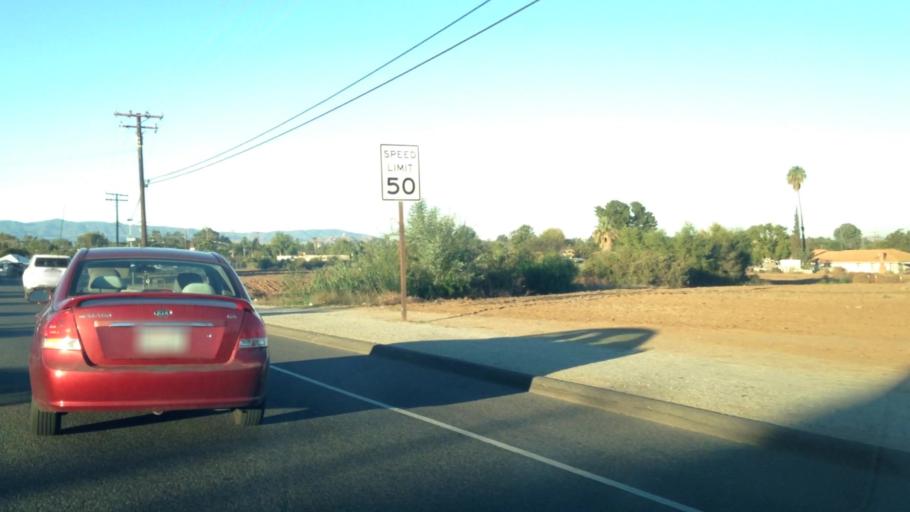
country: US
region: California
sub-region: Riverside County
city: Woodcrest
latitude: 33.8834
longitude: -117.3533
